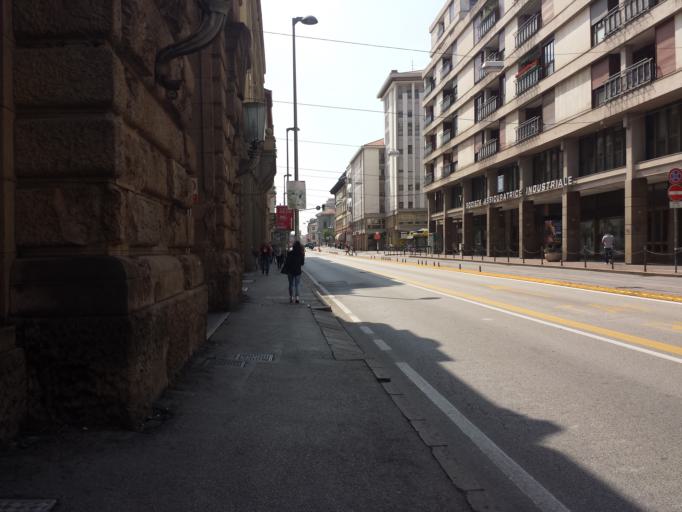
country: IT
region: Veneto
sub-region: Provincia di Padova
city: Padova
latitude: 45.4156
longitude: 11.8792
